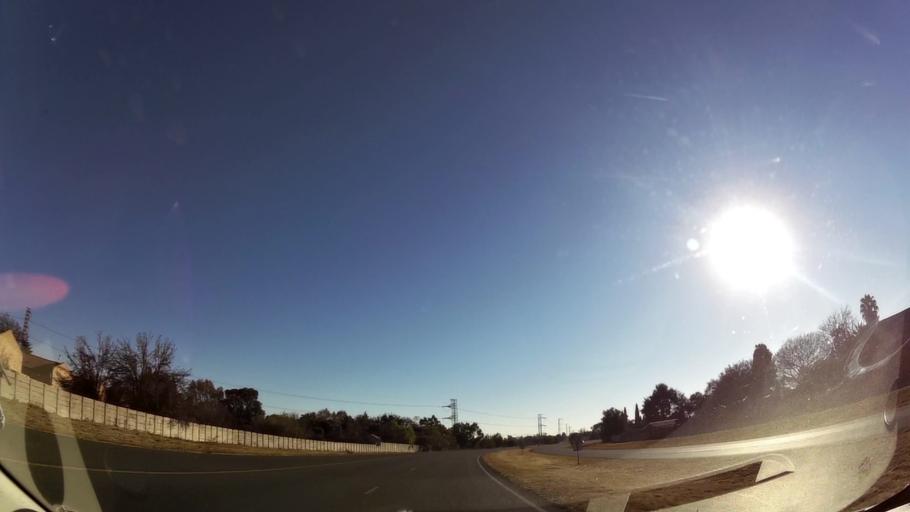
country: ZA
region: Gauteng
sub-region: City of Johannesburg Metropolitan Municipality
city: Modderfontein
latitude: -26.0755
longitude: 28.2031
